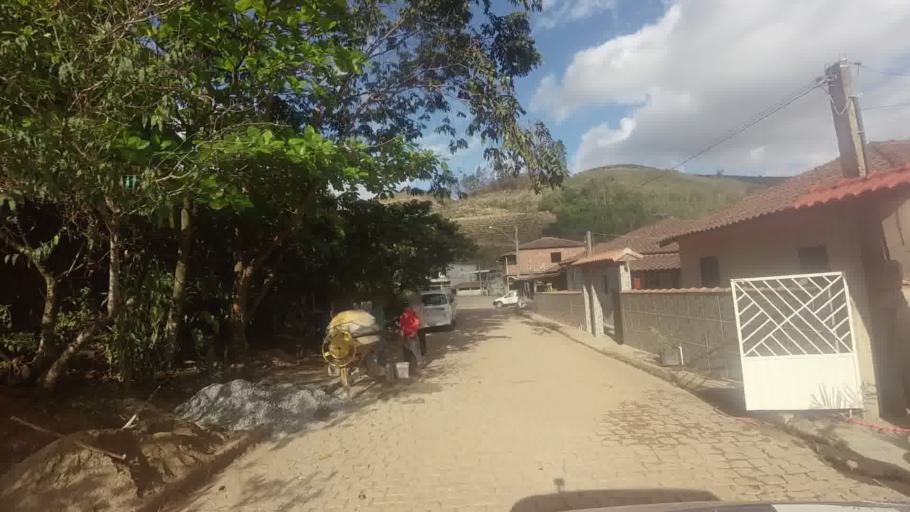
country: BR
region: Espirito Santo
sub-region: Sao Jose Do Calcado
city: Sao Jose do Calcado
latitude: -20.9740
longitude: -41.5104
